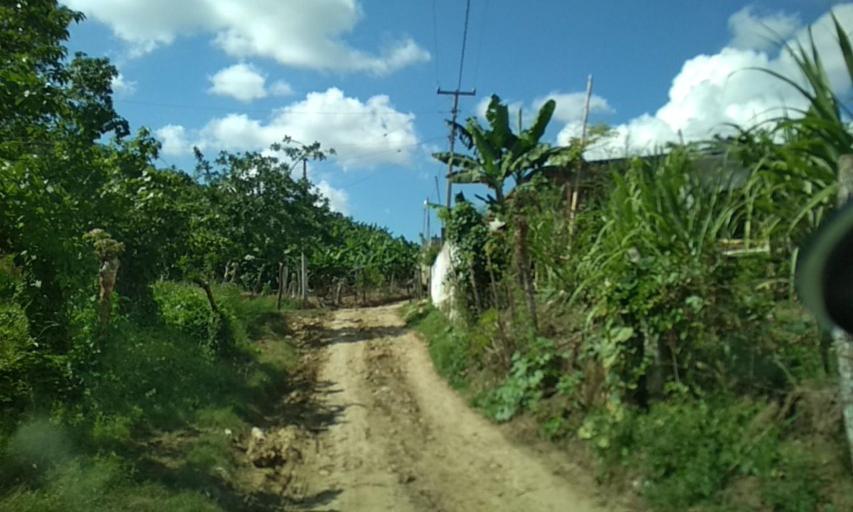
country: MX
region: Veracruz
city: Cazones de Herrera
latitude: 20.6231
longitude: -97.3324
